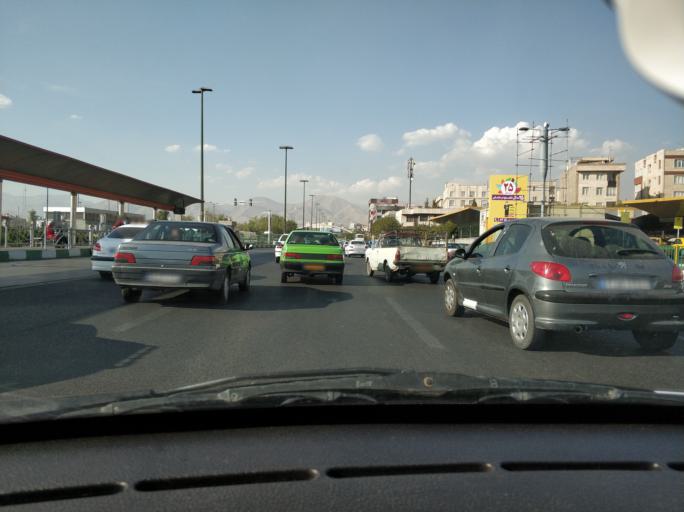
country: IR
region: Tehran
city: Tehran
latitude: 35.7023
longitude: 51.3378
